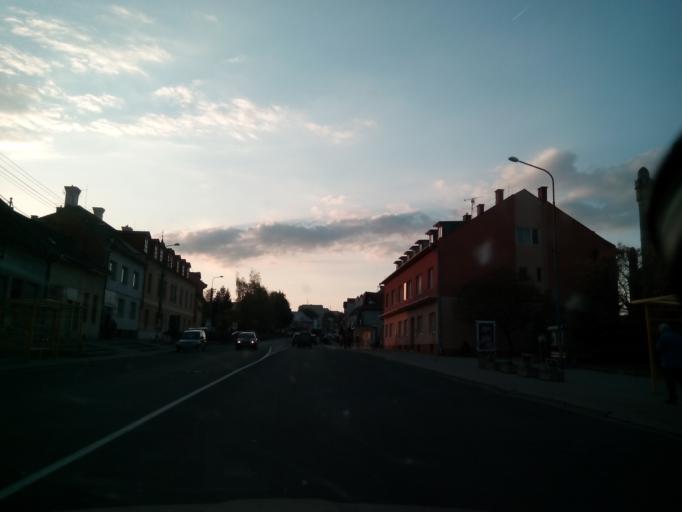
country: SK
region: Trnavsky
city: Vrbove
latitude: 48.6205
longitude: 17.7255
